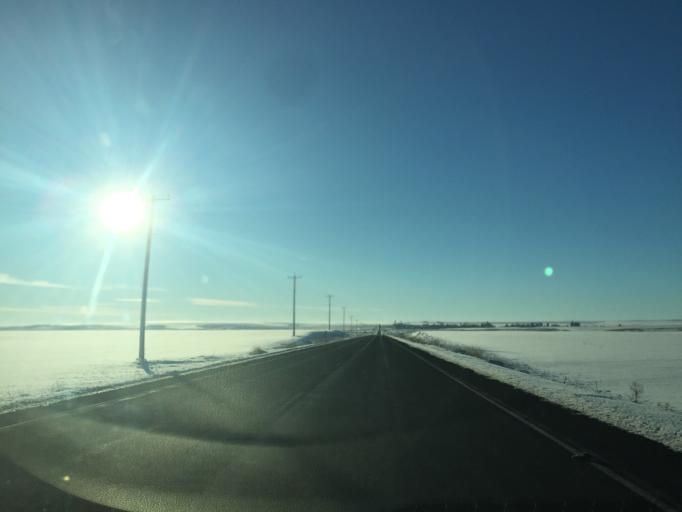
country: US
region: Washington
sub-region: Okanogan County
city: Coulee Dam
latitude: 47.7208
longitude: -118.8966
